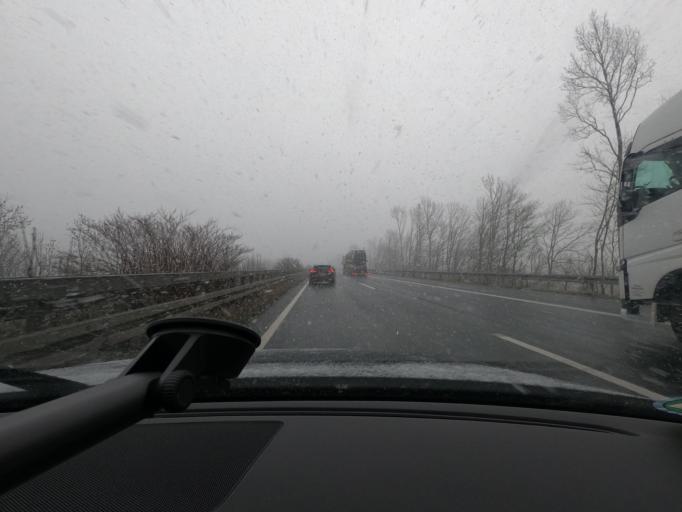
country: DE
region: North Rhine-Westphalia
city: Marsberg
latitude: 51.5459
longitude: 8.8237
